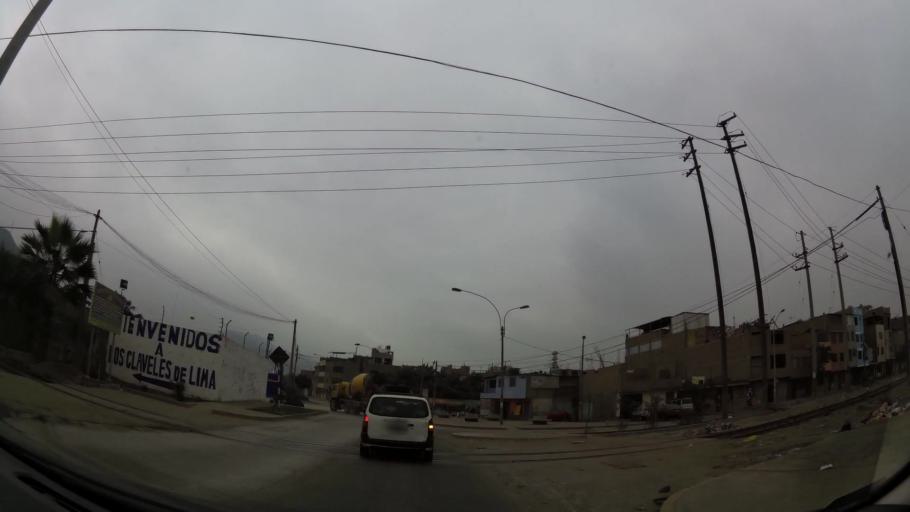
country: PE
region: Lima
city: Lima
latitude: -12.0381
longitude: -77.0057
